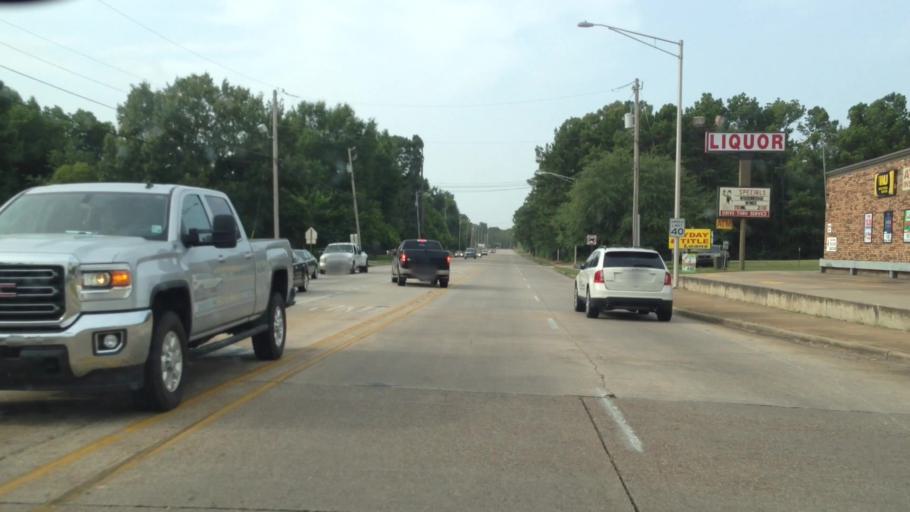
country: US
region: Louisiana
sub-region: De Soto Parish
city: Stonewall
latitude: 32.4020
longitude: -93.8147
